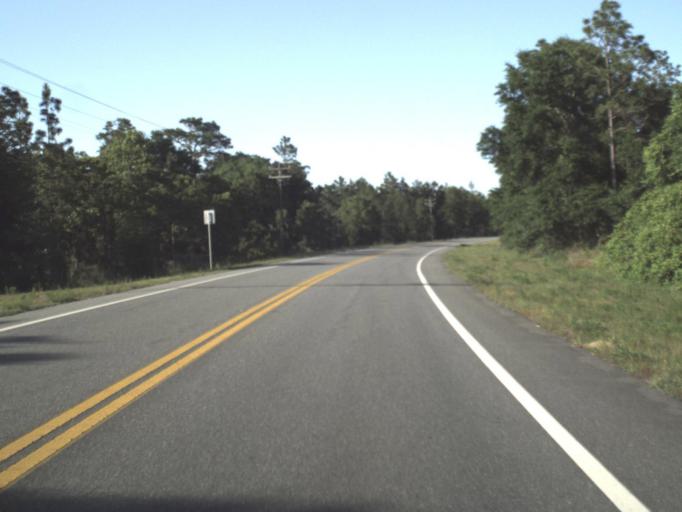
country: US
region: Florida
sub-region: Liberty County
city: Bristol
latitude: 30.4009
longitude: -84.7895
